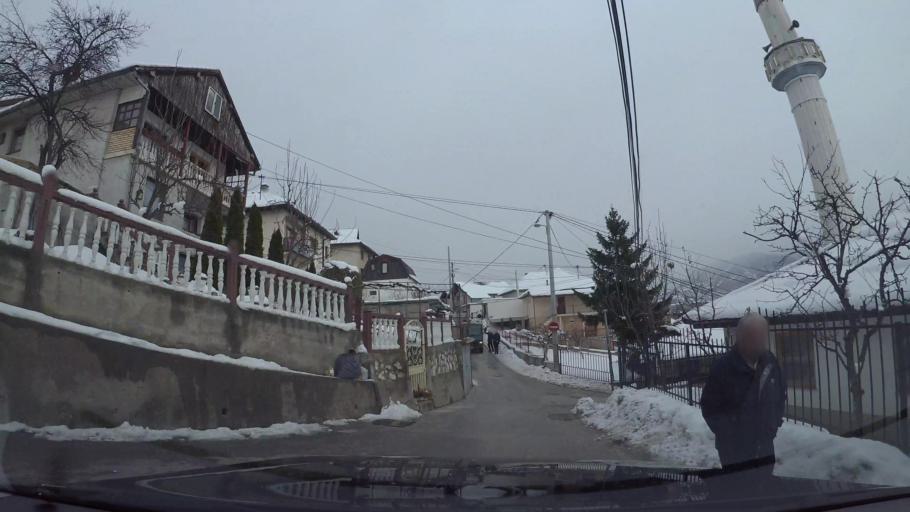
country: BA
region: Federation of Bosnia and Herzegovina
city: Kobilja Glava
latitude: 43.8678
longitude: 18.3971
